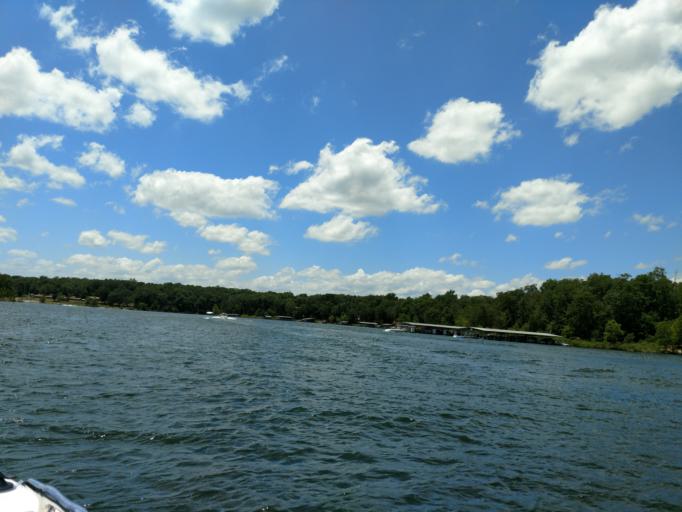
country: US
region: Missouri
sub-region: Barry County
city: Shell Knob
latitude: 36.5856
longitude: -93.5660
